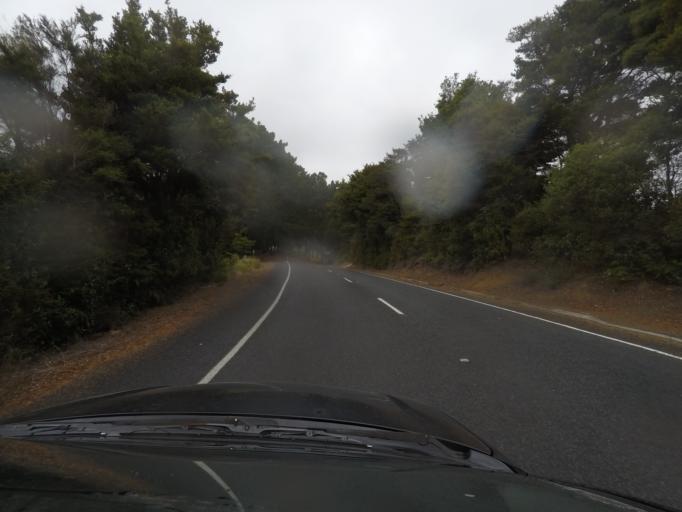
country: NZ
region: Auckland
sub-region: Auckland
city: Warkworth
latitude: -36.2661
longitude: 174.7164
